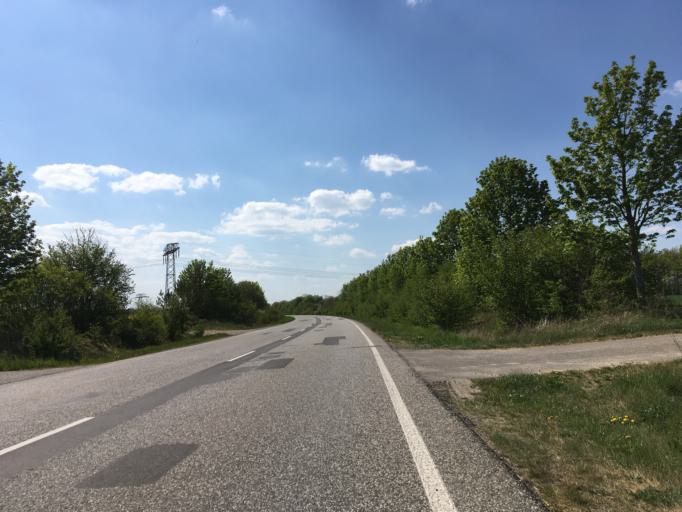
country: DE
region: Brandenburg
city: Werneuchen
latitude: 52.6114
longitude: 13.6604
